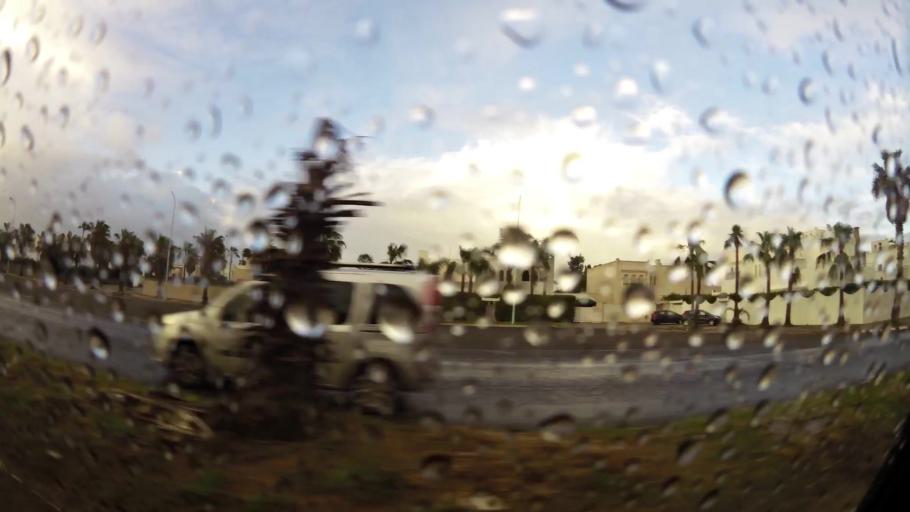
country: MA
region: Doukkala-Abda
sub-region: El-Jadida
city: El Jadida
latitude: 33.2412
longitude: -8.5100
